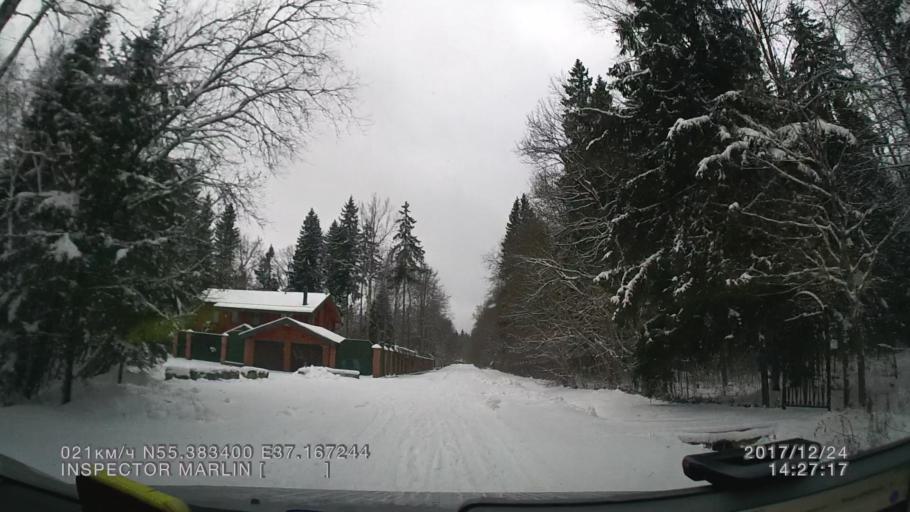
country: RU
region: Moskovskaya
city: Troitsk
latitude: 55.3833
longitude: 37.1671
